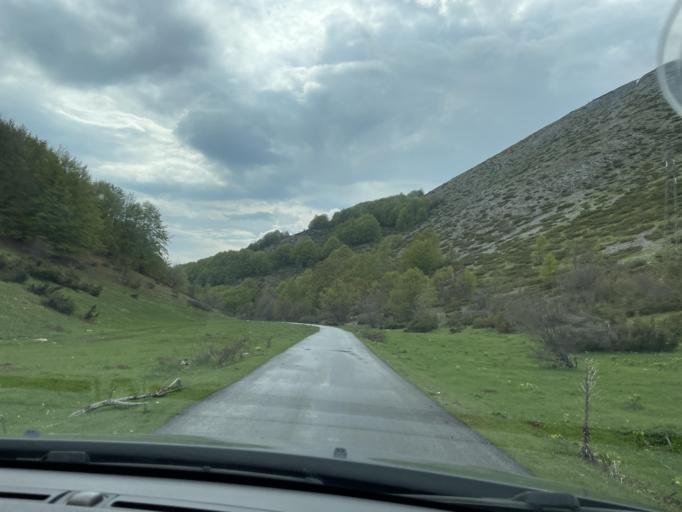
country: MK
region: Opstina Rostusa
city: Rostusha
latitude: 41.6012
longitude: 20.6792
